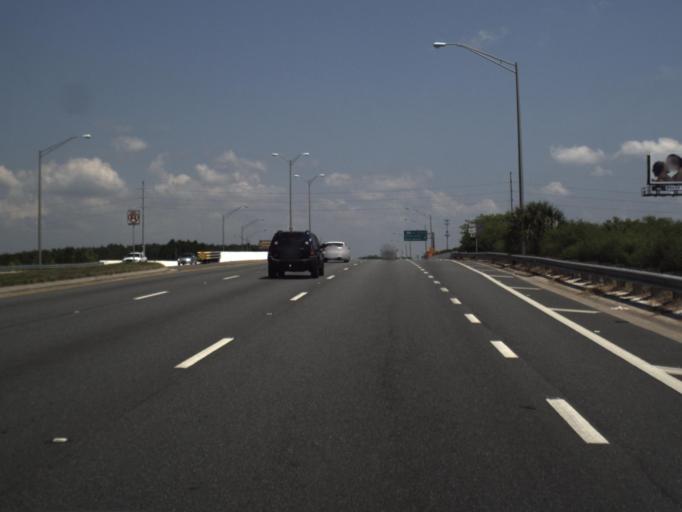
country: US
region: Florida
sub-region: Hillsborough County
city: Egypt Lake-Leto
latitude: 28.0351
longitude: -82.5048
